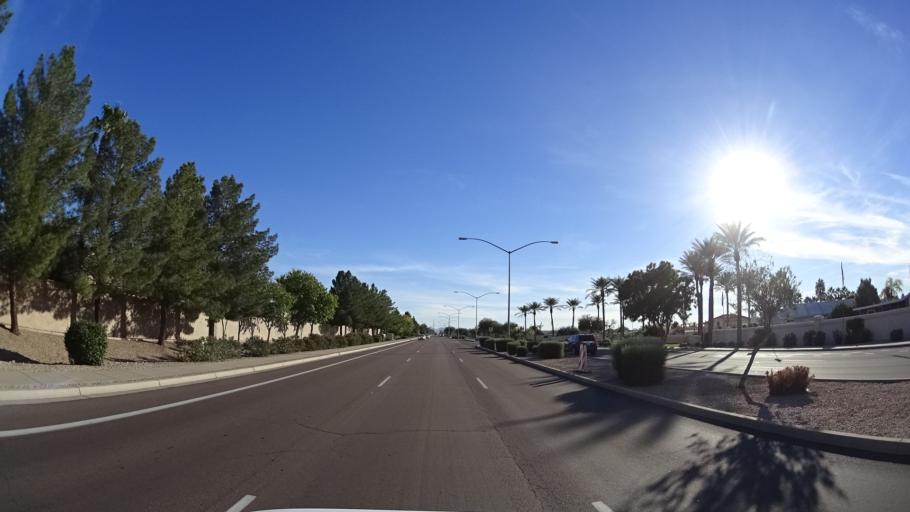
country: US
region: Arizona
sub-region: Pinal County
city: Apache Junction
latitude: 33.3702
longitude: -111.6360
